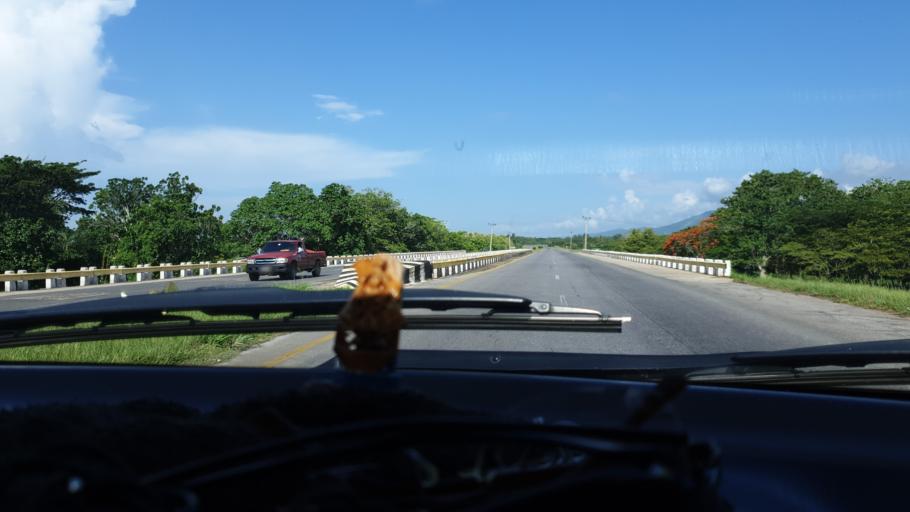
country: CU
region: Artemisa
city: San Cristobal
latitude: 22.7221
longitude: -83.0417
